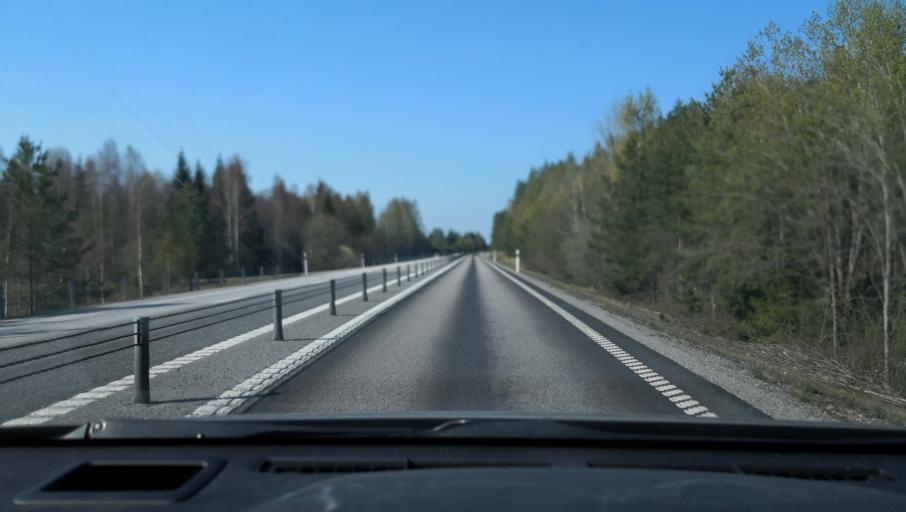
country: SE
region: Uppsala
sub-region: Heby Kommun
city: Tarnsjo
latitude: 60.2147
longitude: 16.9529
